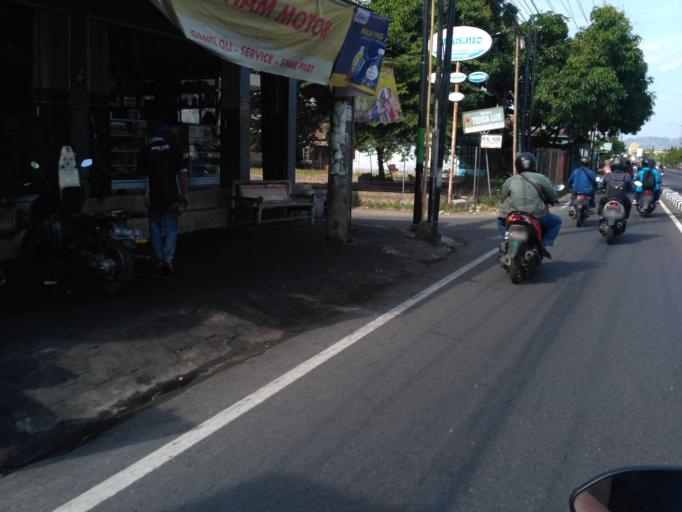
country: ID
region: Daerah Istimewa Yogyakarta
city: Depok
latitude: -7.7647
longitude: 110.4250
